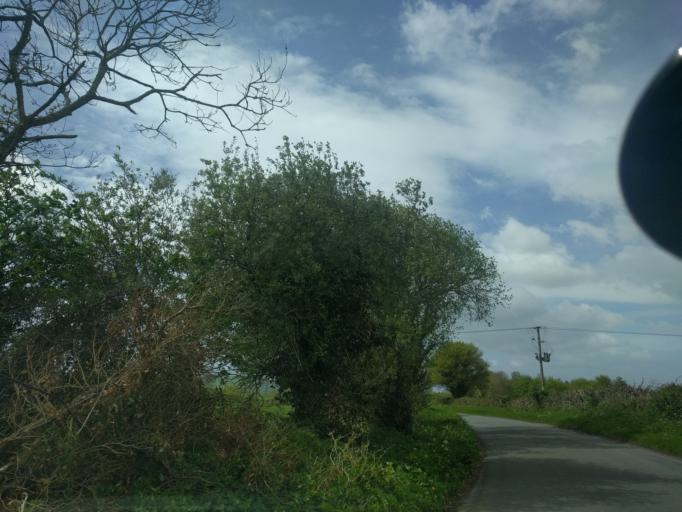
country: GB
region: England
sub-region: Wiltshire
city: Edington
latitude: 51.2835
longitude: -2.1045
